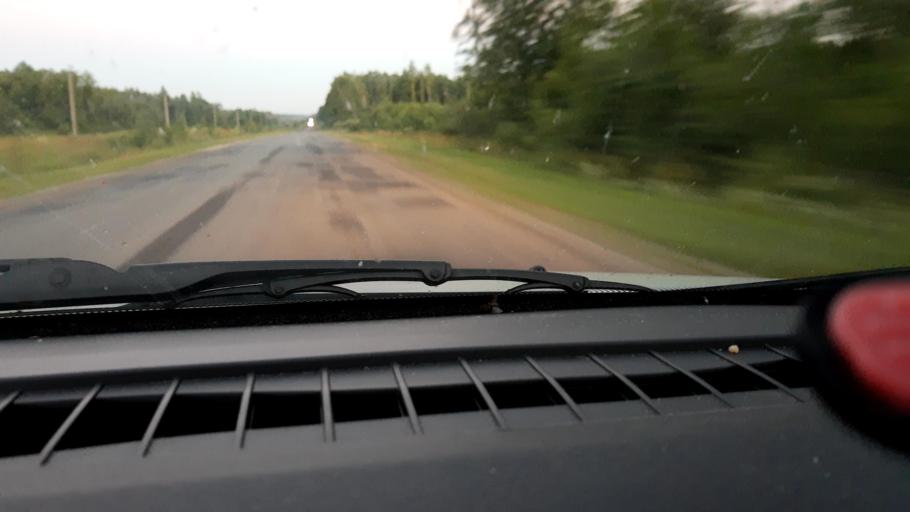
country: RU
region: Nizjnij Novgorod
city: Prudy
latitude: 57.4730
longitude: 46.0396
